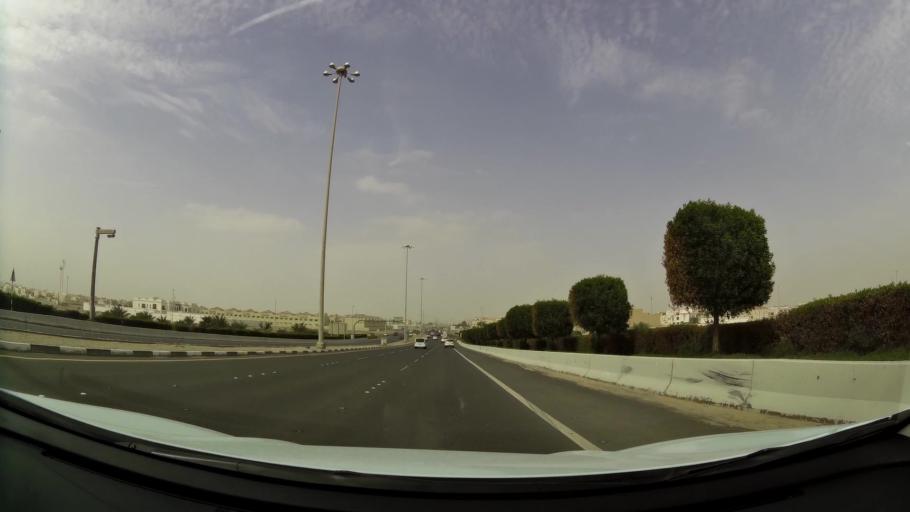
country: AE
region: Abu Dhabi
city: Abu Dhabi
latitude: 24.3993
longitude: 54.5739
